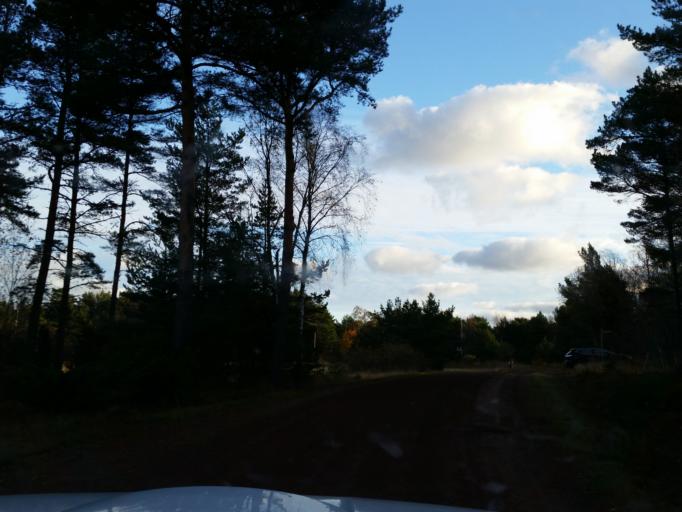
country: AX
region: Alands skaergard
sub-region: Foegloe
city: Foegloe
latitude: 59.9941
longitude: 20.3264
